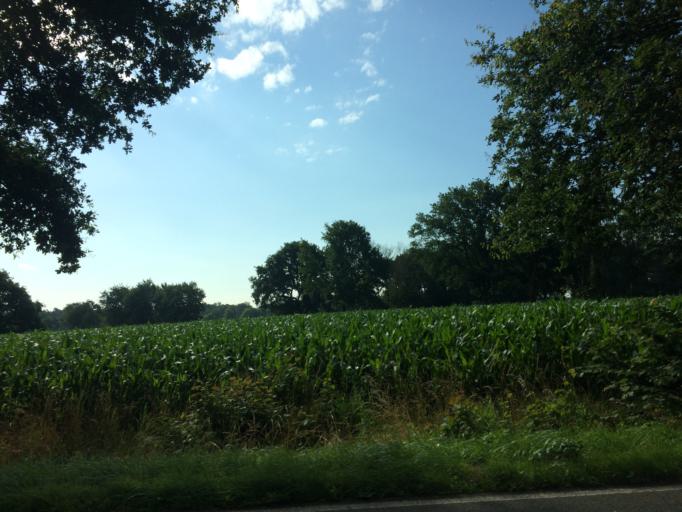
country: DE
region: North Rhine-Westphalia
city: Dorsten
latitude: 51.6989
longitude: 7.0040
